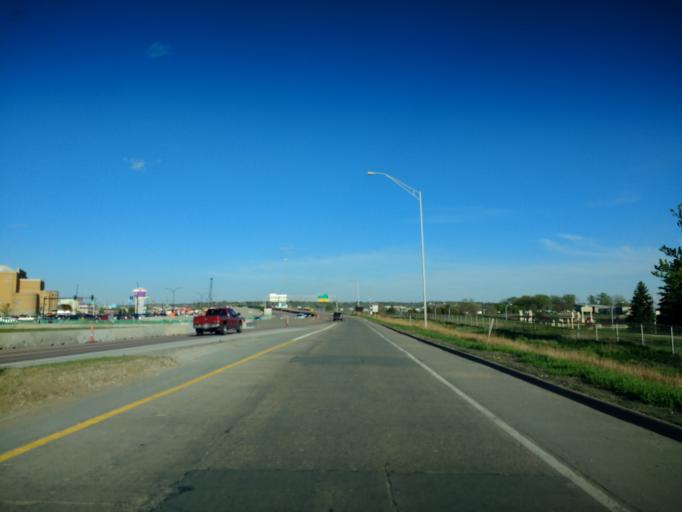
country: US
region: Iowa
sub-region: Woodbury County
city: Sioux City
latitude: 42.4903
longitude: -96.4102
